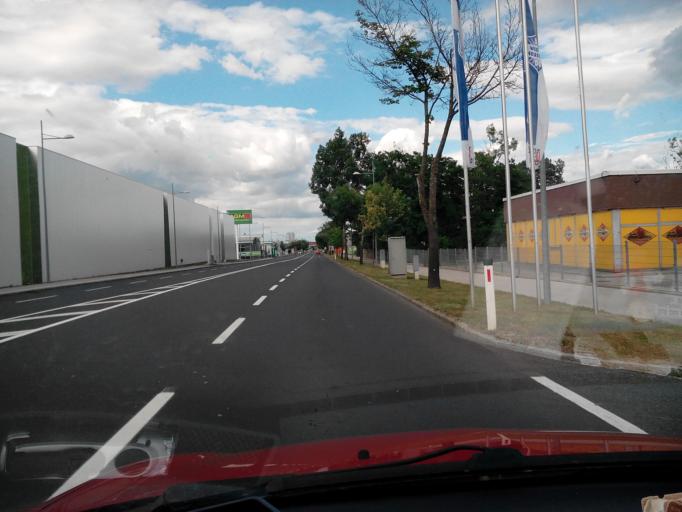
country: AT
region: Lower Austria
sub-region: Wiener Neustadt Stadt
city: Wiener Neustadt
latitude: 47.7967
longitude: 16.2215
